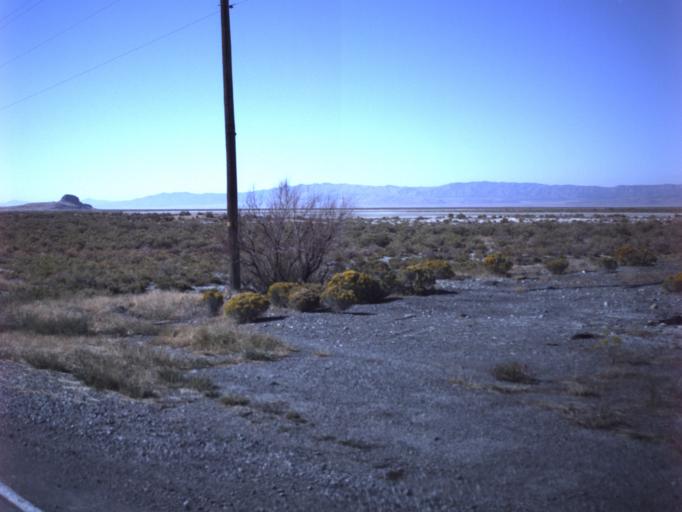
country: US
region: Utah
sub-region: Tooele County
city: Grantsville
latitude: 40.7432
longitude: -112.6537
